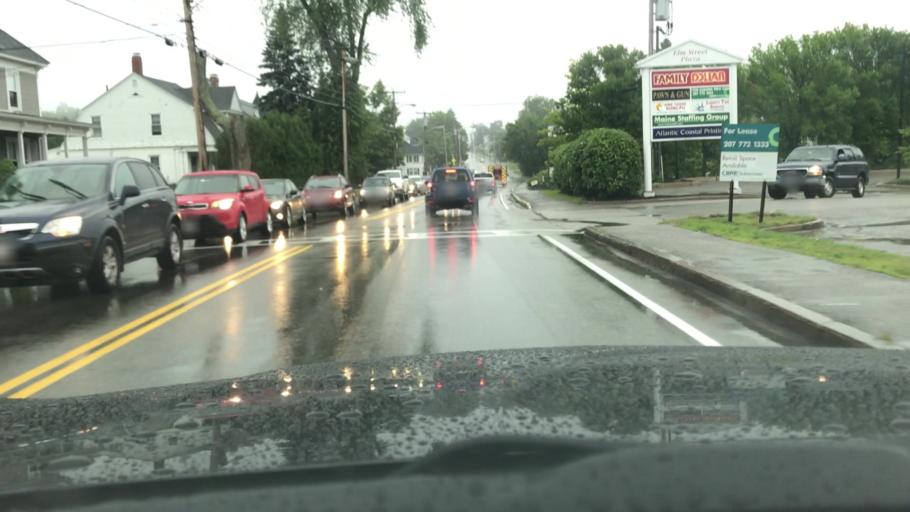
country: US
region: Maine
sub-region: York County
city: Biddeford
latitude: 43.4871
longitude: -70.4673
